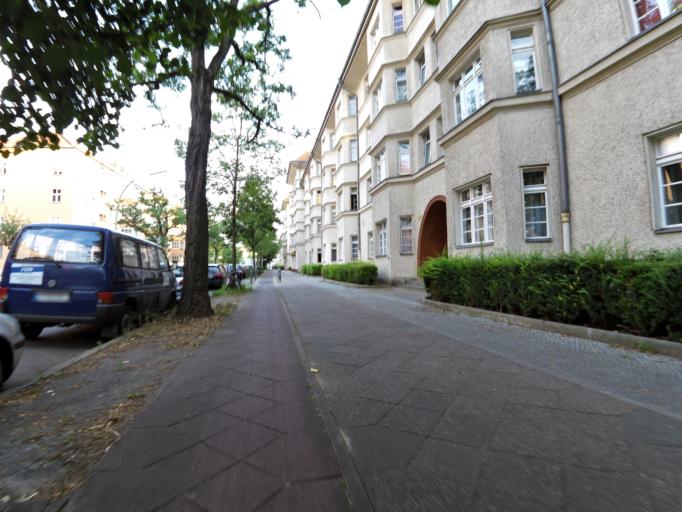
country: DE
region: Berlin
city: Schoneberg Bezirk
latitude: 52.4742
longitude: 13.3433
